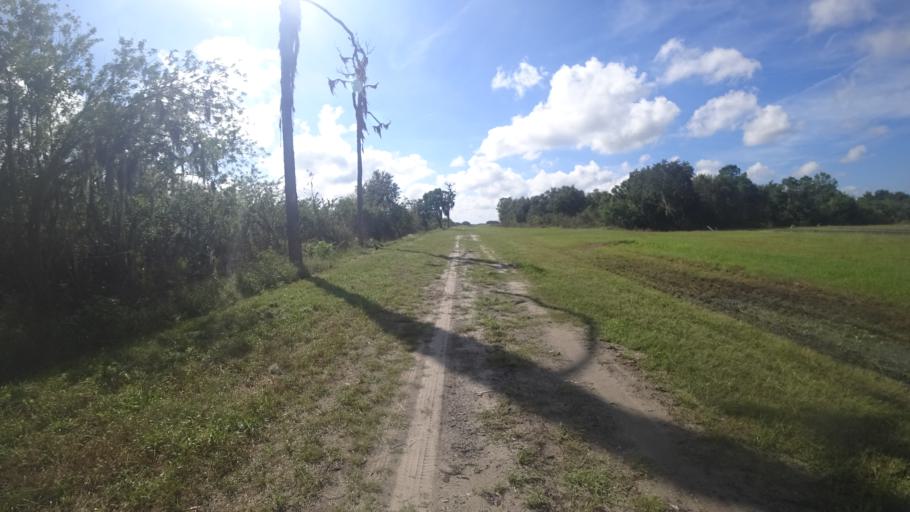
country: US
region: Florida
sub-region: Hillsborough County
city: Ruskin
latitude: 27.6425
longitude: -82.4971
